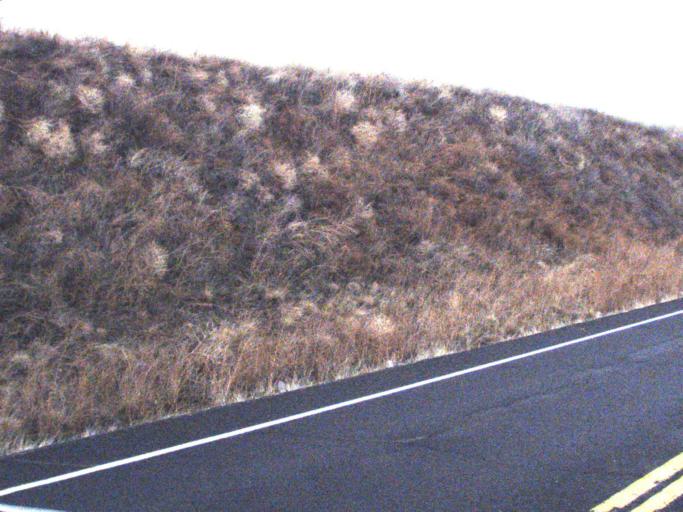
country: US
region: Washington
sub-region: Walla Walla County
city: Waitsburg
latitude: 46.2501
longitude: -118.1471
